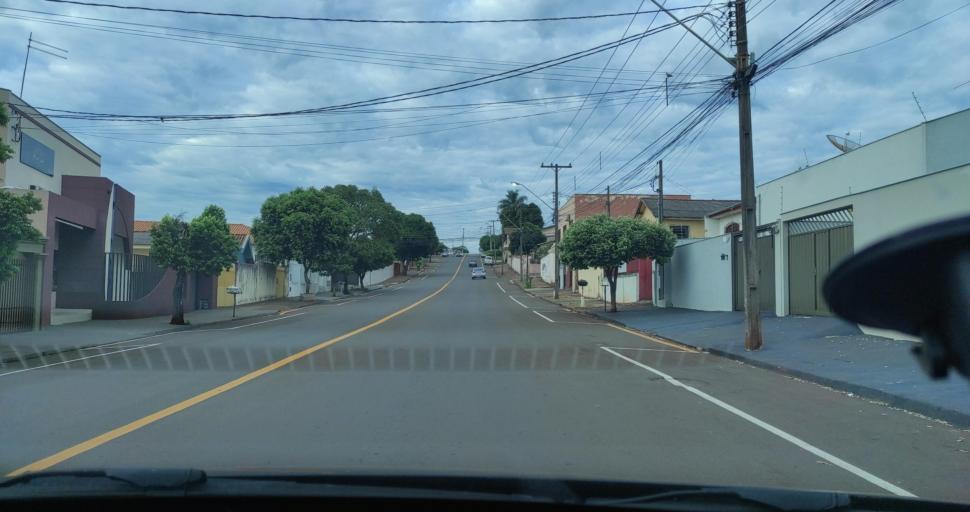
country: BR
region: Parana
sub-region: Ibipora
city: Ibipora
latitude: -23.2654
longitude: -51.0449
